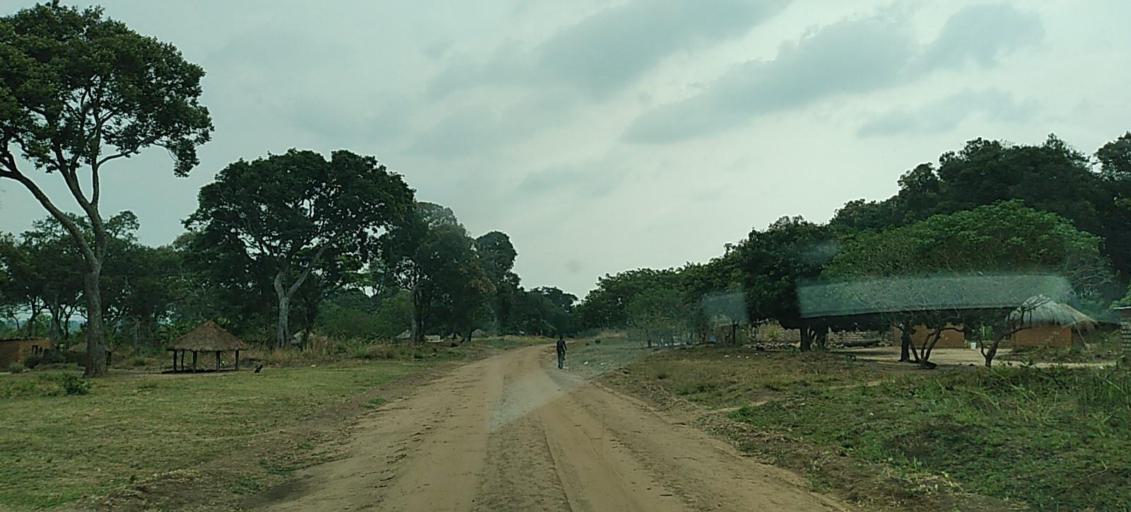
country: ZM
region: North-Western
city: Mwinilunga
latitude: -11.4199
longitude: 24.5984
